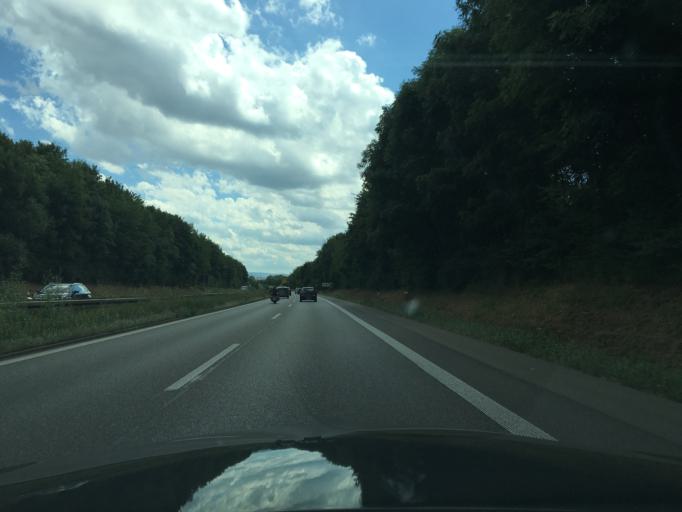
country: DE
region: Baden-Wuerttemberg
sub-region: Regierungsbezirk Stuttgart
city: Leinfelden-Echterdingen
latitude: 48.6811
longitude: 9.1810
